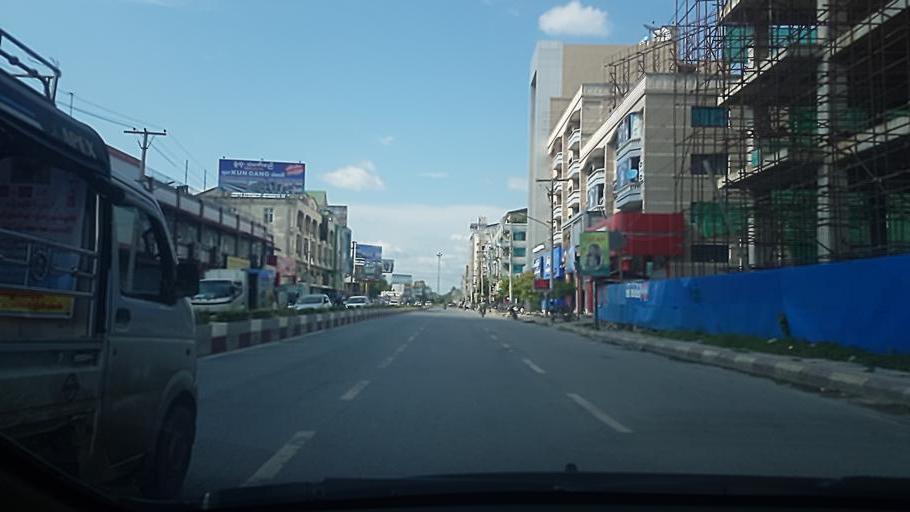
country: MM
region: Mandalay
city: Mandalay
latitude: 21.9742
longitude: 96.0869
